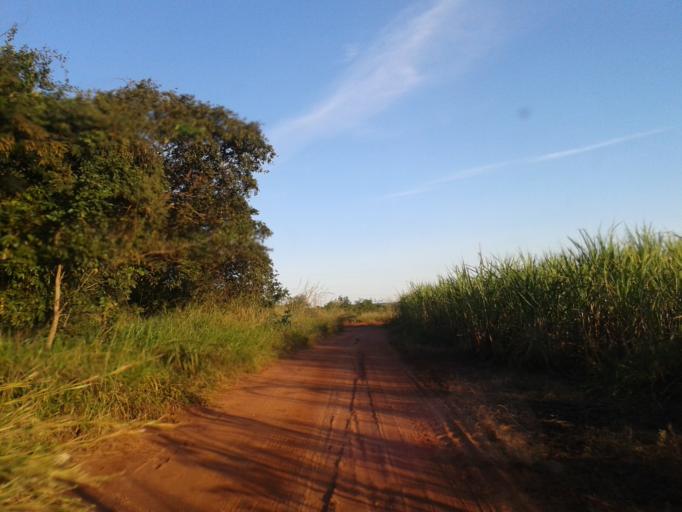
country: BR
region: Minas Gerais
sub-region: Santa Vitoria
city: Santa Vitoria
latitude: -19.0093
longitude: -50.3773
